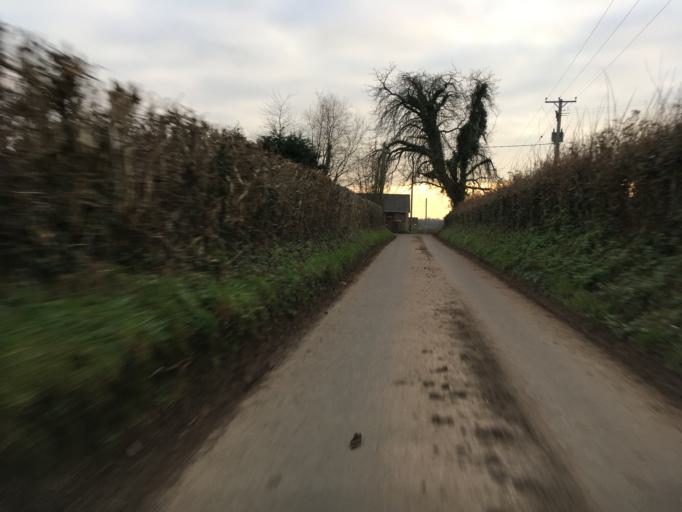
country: GB
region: Wales
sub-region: Newport
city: Marshfield
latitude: 51.5438
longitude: -3.0929
